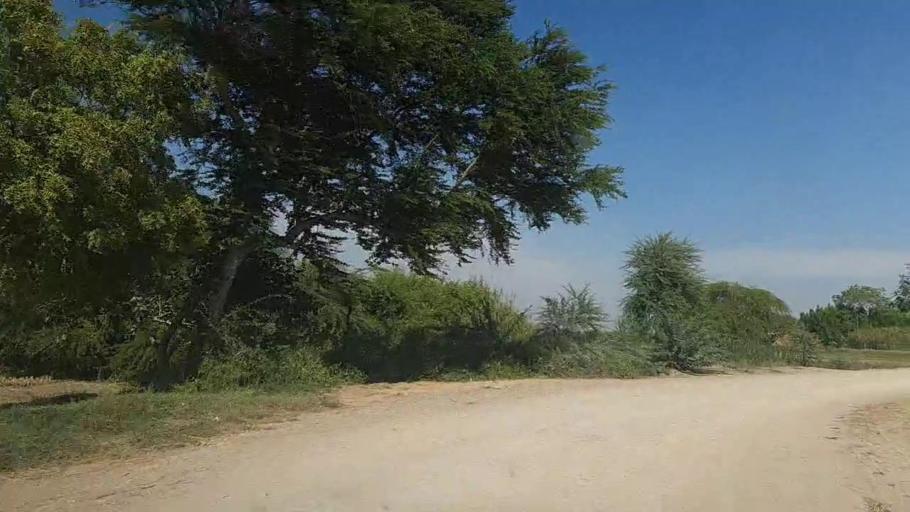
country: PK
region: Sindh
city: Mirpur Batoro
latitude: 24.7507
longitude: 68.2827
